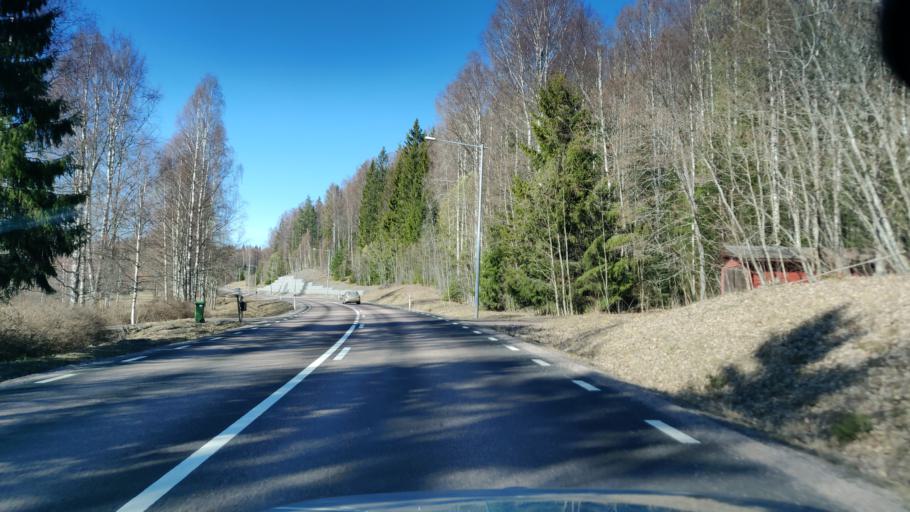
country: SE
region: Vaermland
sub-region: Hagfors Kommun
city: Hagfors
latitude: 59.9396
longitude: 13.6784
